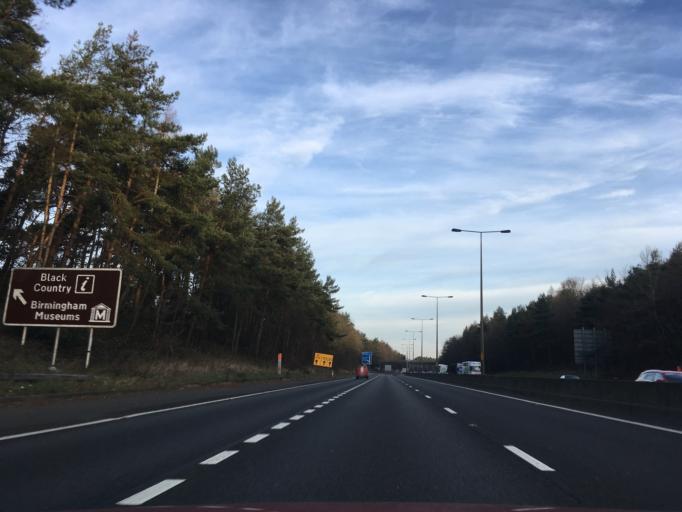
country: GB
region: England
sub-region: City and Borough of Birmingham
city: Bartley Green
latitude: 52.4402
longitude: -2.0180
